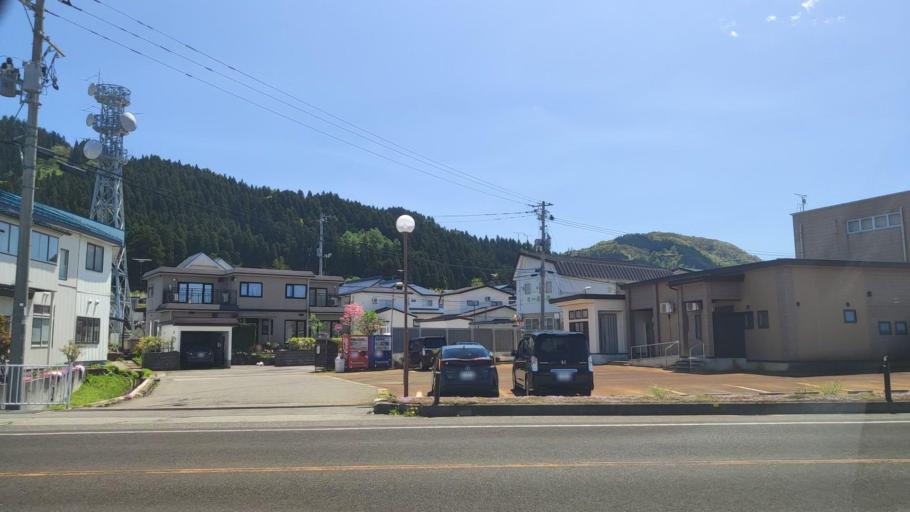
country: JP
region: Akita
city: Yuzawa
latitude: 39.1423
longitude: 140.4883
